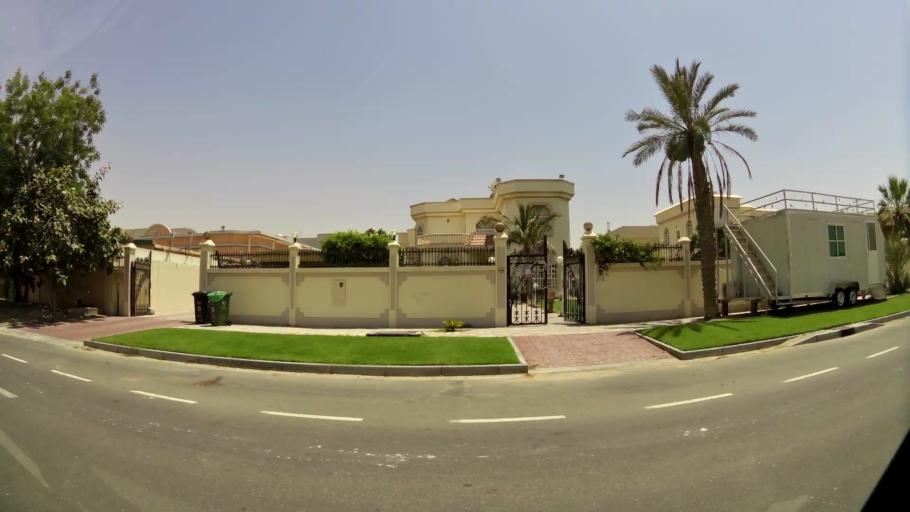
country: AE
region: Dubai
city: Dubai
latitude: 25.0884
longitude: 55.2020
